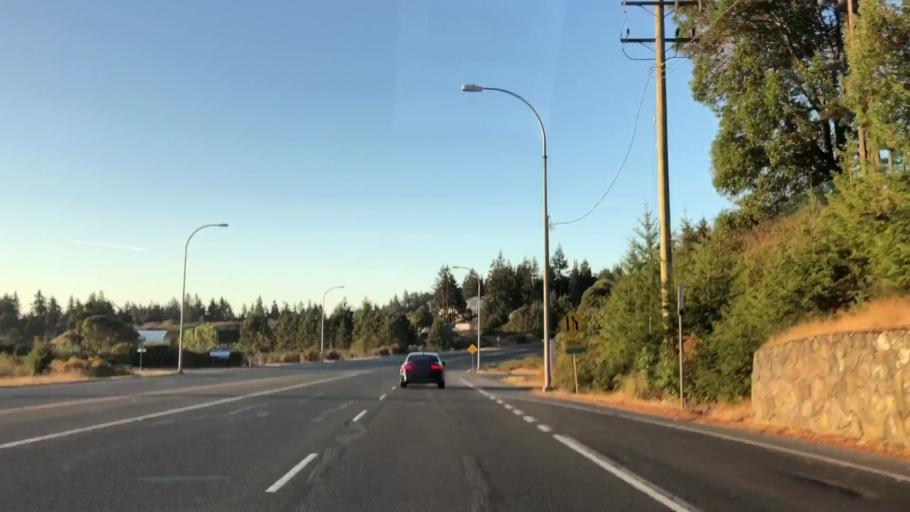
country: CA
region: British Columbia
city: Colwood
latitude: 48.4281
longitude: -123.5023
